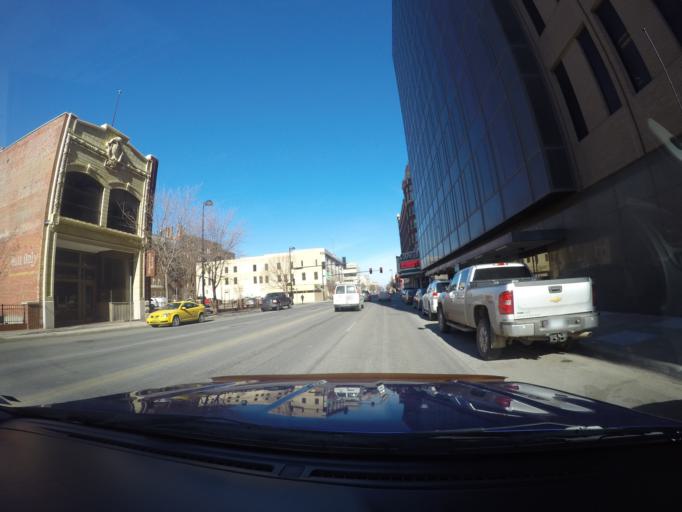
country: US
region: Kansas
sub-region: Sedgwick County
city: Wichita
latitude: 37.6874
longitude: -97.3356
